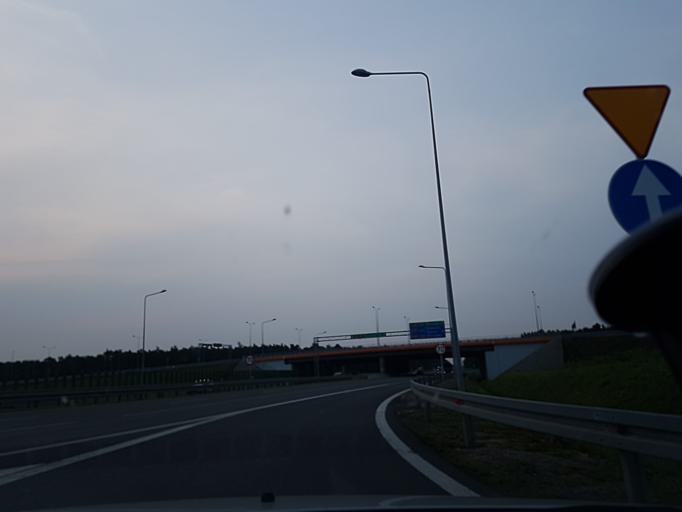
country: PL
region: Lodz Voivodeship
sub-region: Powiat lodzki wschodni
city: Rzgow
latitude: 51.6395
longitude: 19.4979
